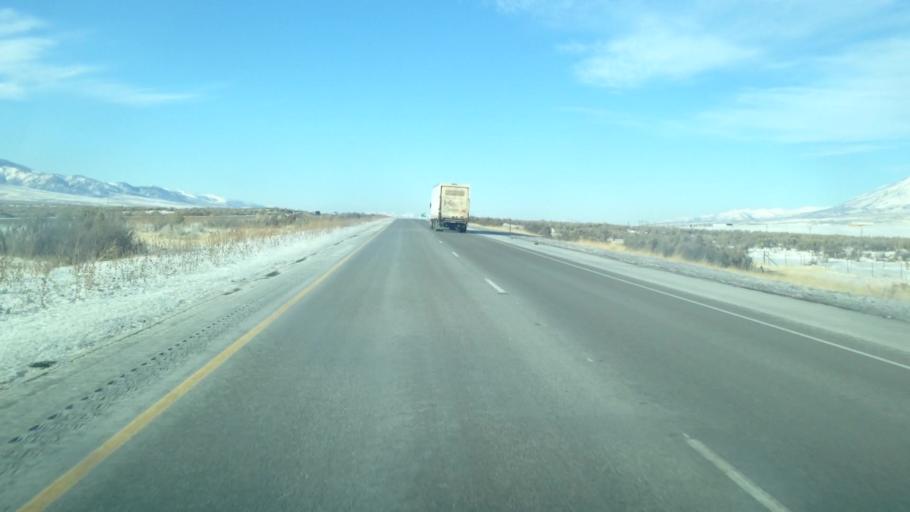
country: US
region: Idaho
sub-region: Bannock County
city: Pocatello
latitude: 42.5933
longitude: -112.1898
